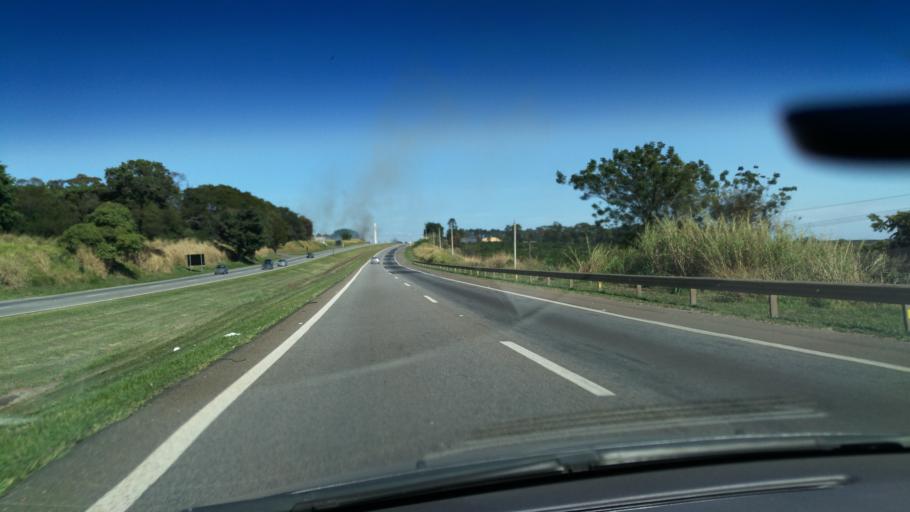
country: BR
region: Sao Paulo
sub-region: Mogi-Mirim
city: Mogi Mirim
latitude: -22.4984
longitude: -46.9840
